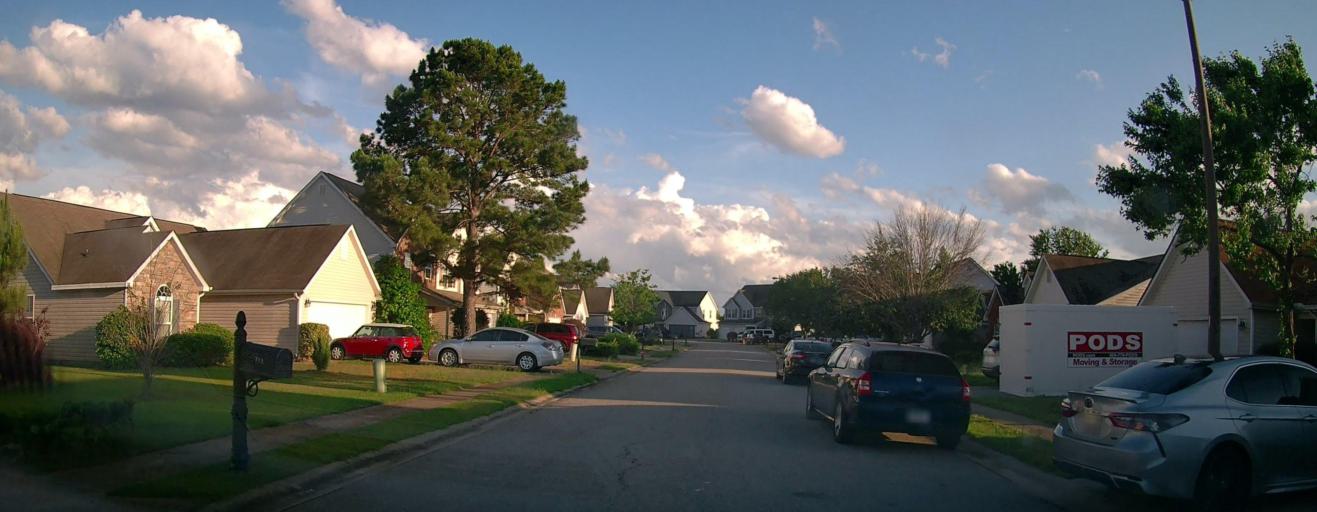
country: US
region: Georgia
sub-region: Houston County
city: Centerville
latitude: 32.6303
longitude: -83.7134
